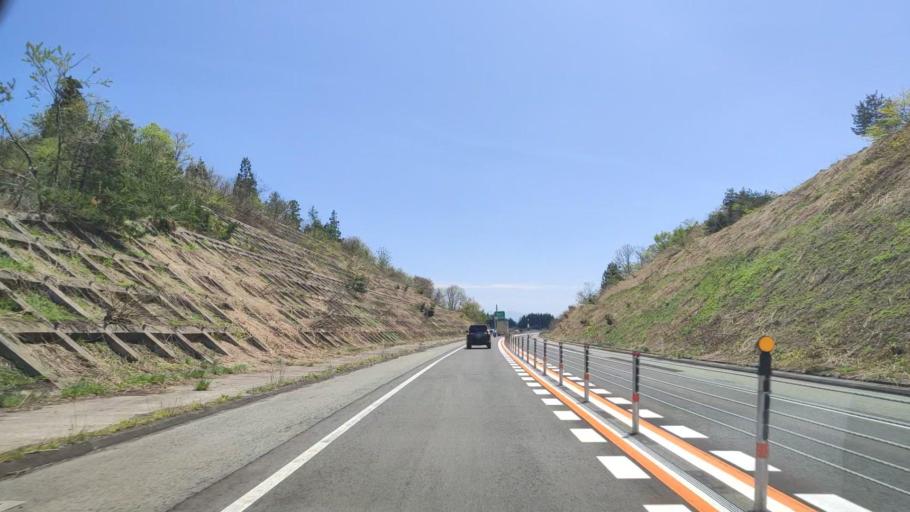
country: JP
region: Yamagata
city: Obanazawa
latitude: 38.6438
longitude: 140.3733
